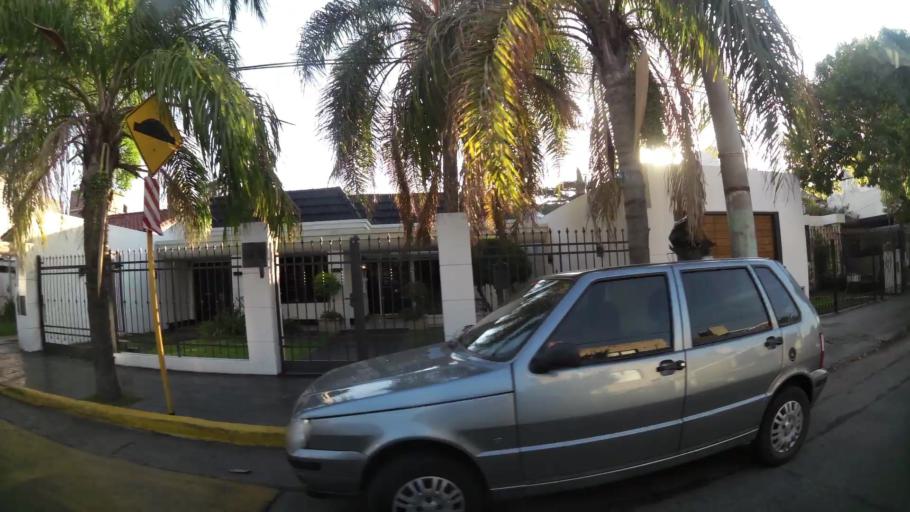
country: AR
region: Cordoba
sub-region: Departamento de Capital
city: Cordoba
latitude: -31.3759
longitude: -64.2306
